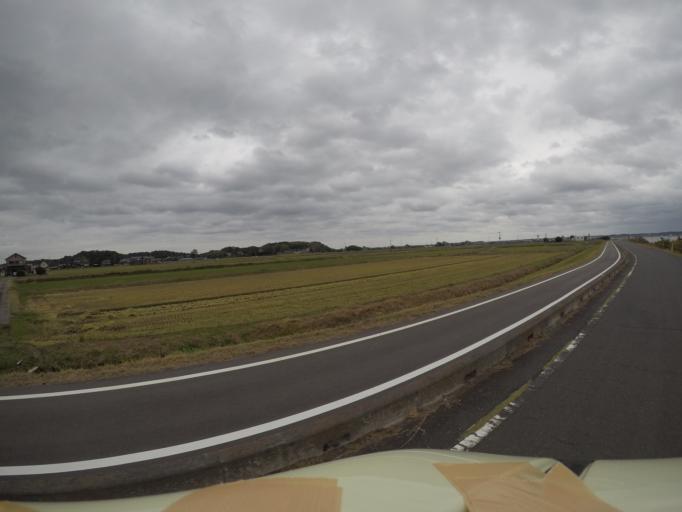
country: JP
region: Ibaraki
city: Inashiki
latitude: 36.0762
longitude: 140.3819
